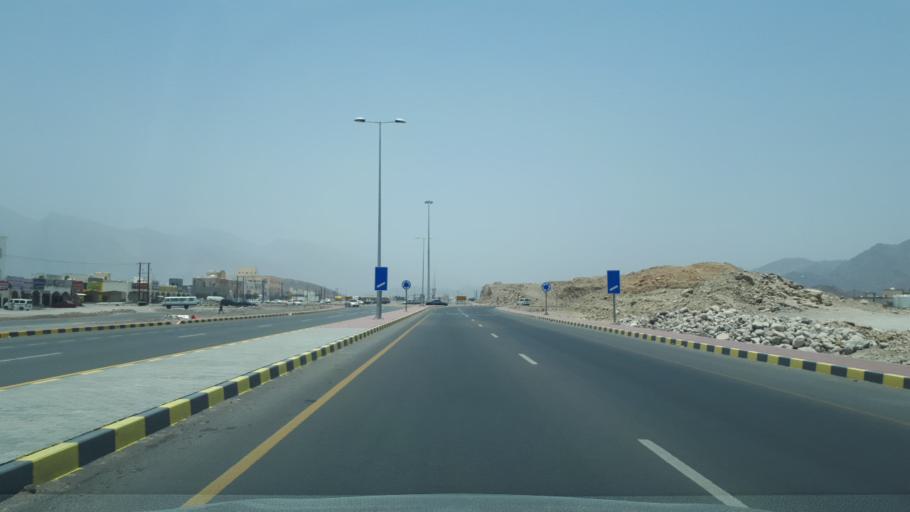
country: OM
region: Al Batinah
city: Rustaq
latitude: 23.4351
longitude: 57.3911
